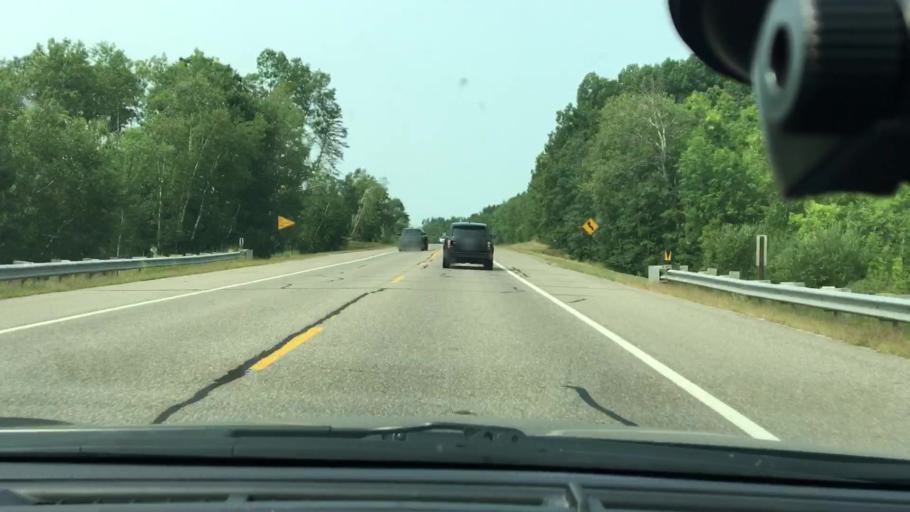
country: US
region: Minnesota
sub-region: Cass County
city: East Gull Lake
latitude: 46.3839
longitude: -94.3157
